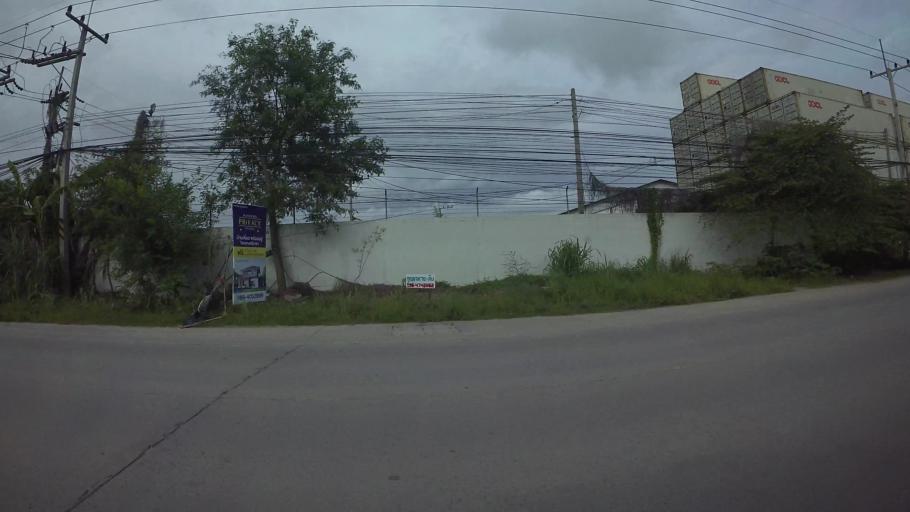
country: TH
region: Chon Buri
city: Ban Talat Bueng
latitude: 13.1246
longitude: 100.9718
